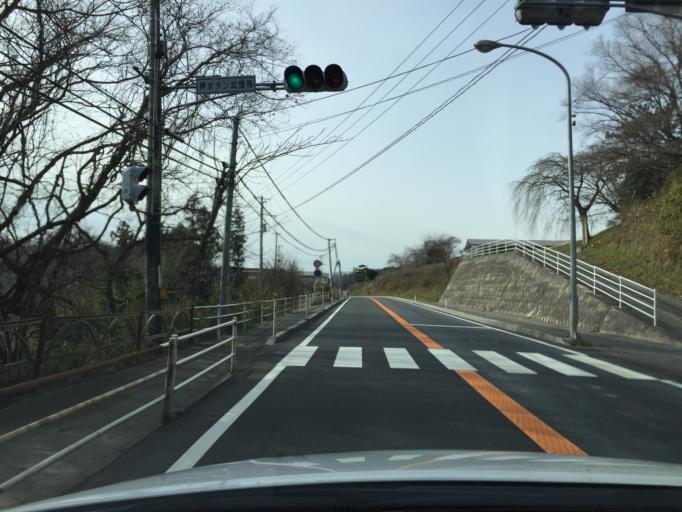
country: JP
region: Fukushima
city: Funehikimachi-funehiki
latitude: 37.4373
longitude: 140.5487
